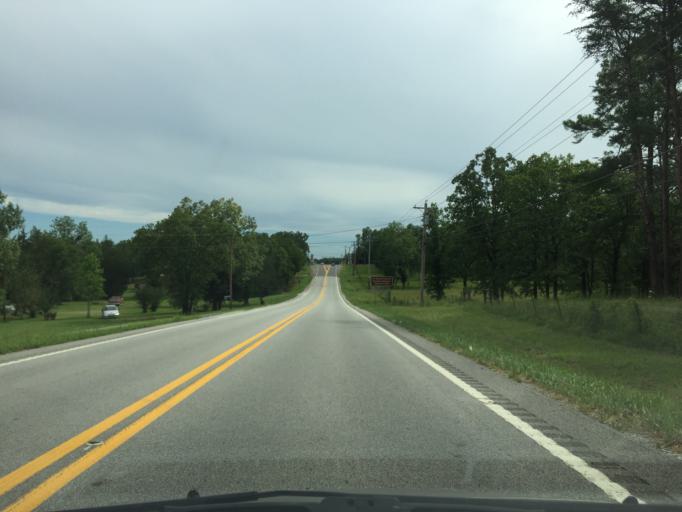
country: US
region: Tennessee
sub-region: Bradley County
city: Hopewell
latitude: 35.2975
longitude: -84.9624
